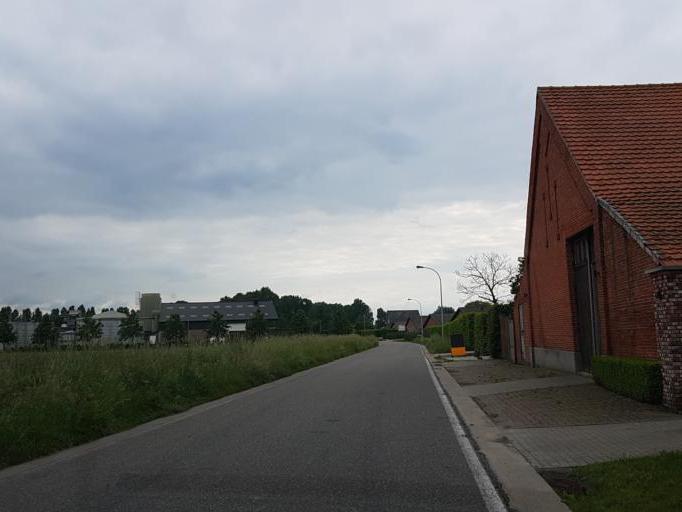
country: BE
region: Flanders
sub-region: Provincie Antwerpen
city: Hoogstraten
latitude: 51.3900
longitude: 4.8134
